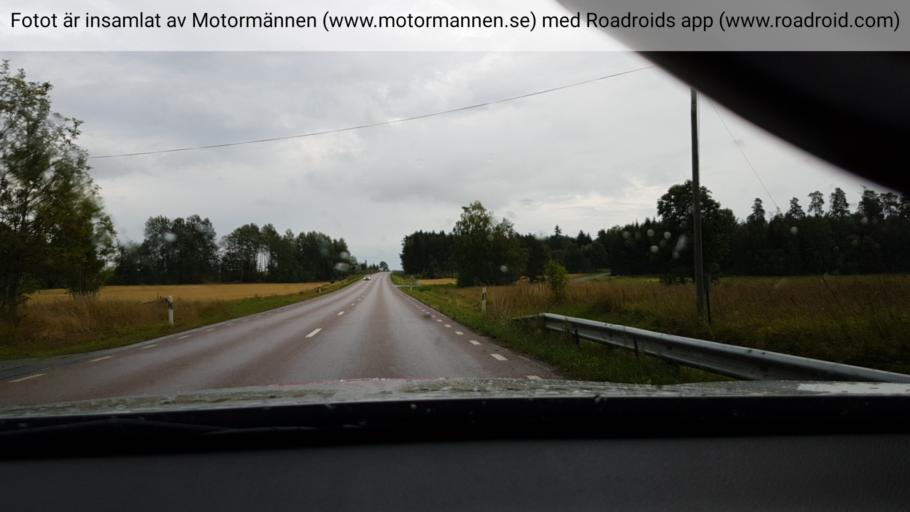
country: SE
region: Uppsala
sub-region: Tierps Kommun
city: Karlholmsbruk
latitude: 60.4390
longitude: 17.7839
